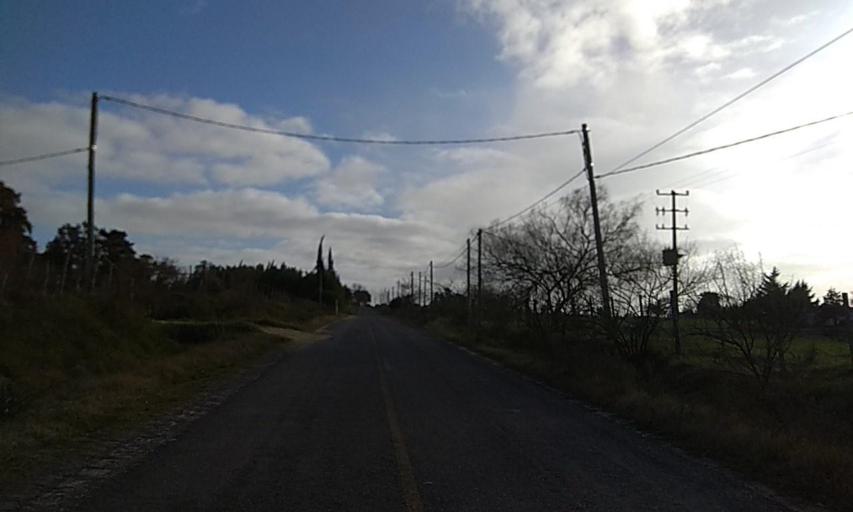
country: UY
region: Florida
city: Florida
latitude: -34.0479
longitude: -56.1892
